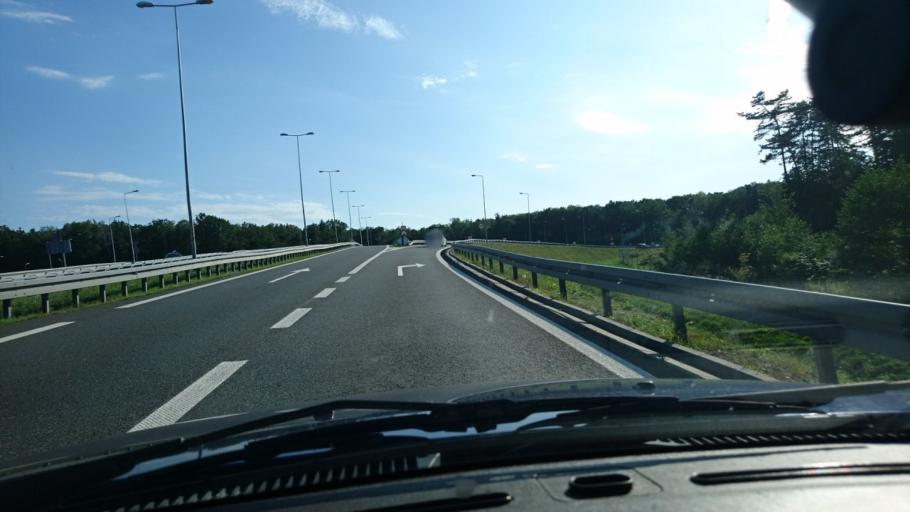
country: PL
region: Silesian Voivodeship
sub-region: Gliwice
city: Gliwice
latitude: 50.3093
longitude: 18.7218
